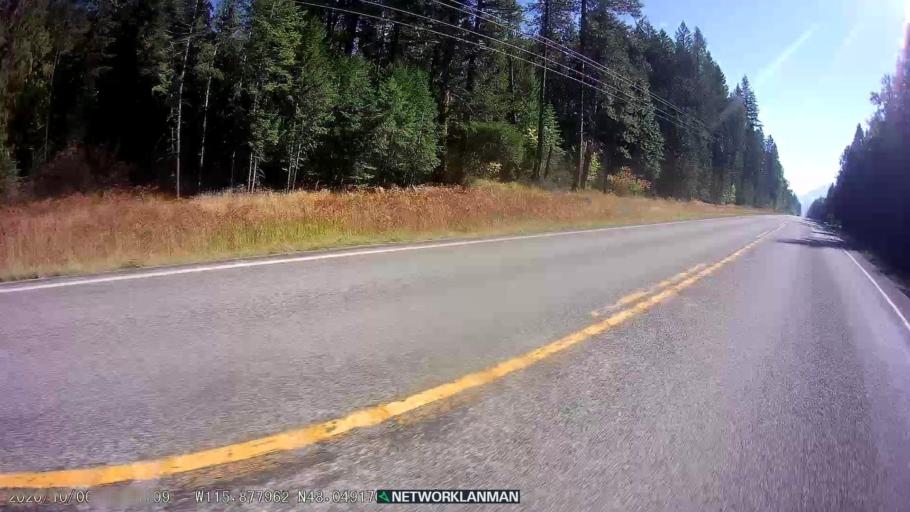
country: US
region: Montana
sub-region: Lincoln County
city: Libby
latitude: 48.0489
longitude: -115.8777
